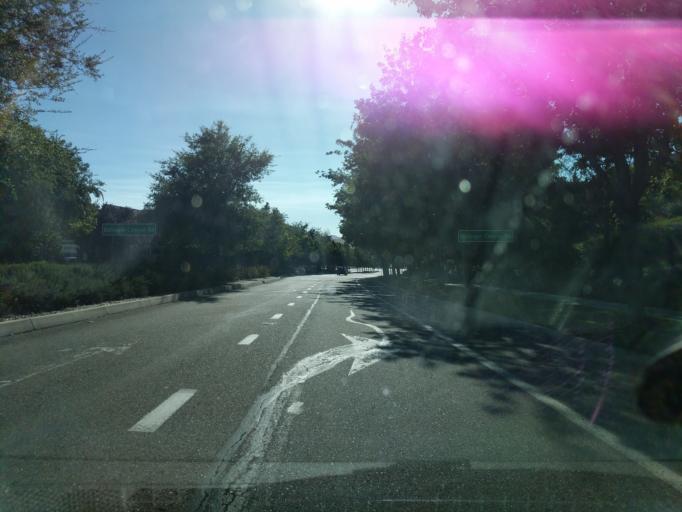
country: US
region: California
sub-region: Contra Costa County
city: Blackhawk
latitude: 37.7633
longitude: -121.9013
